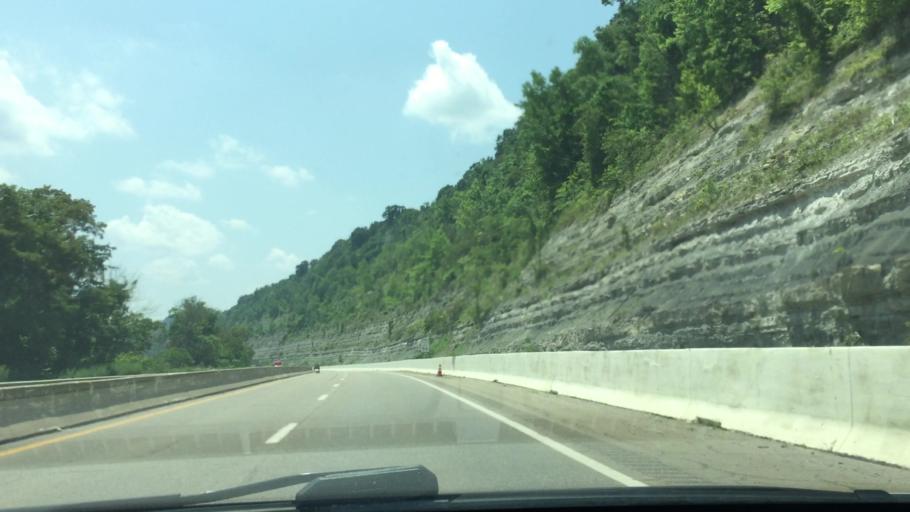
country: US
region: West Virginia
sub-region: Marshall County
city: Glendale
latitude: 39.9523
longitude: -80.7645
